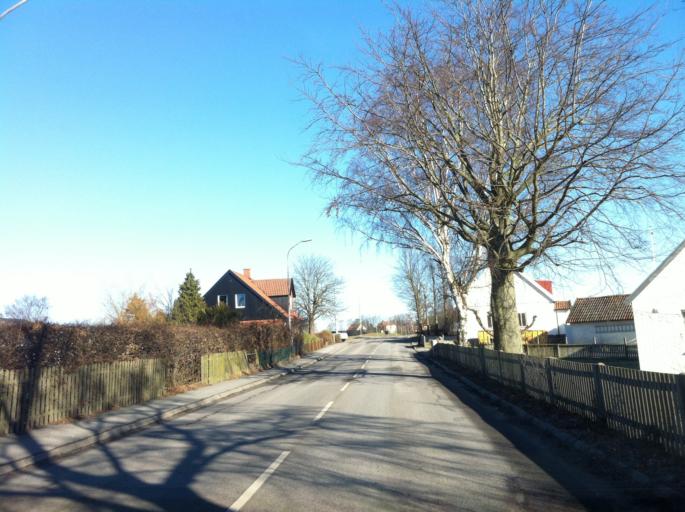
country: SE
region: Skane
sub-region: Svedala Kommun
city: Klagerup
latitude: 55.5735
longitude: 13.1981
